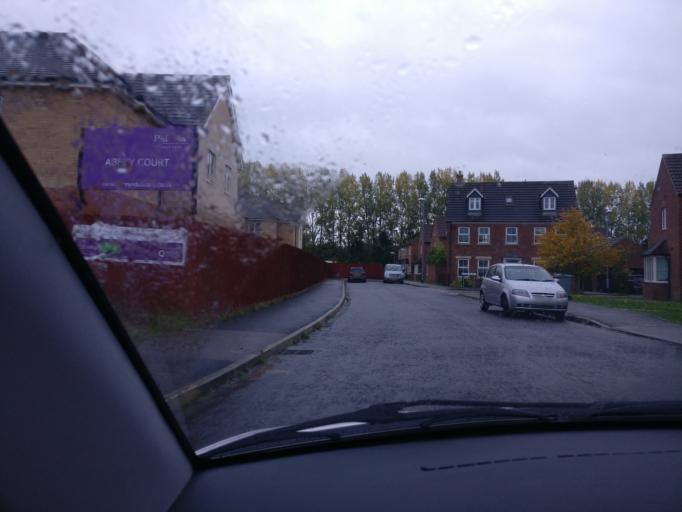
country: GB
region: England
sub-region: Lincolnshire
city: Bourne
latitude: 52.7581
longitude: -0.3670
